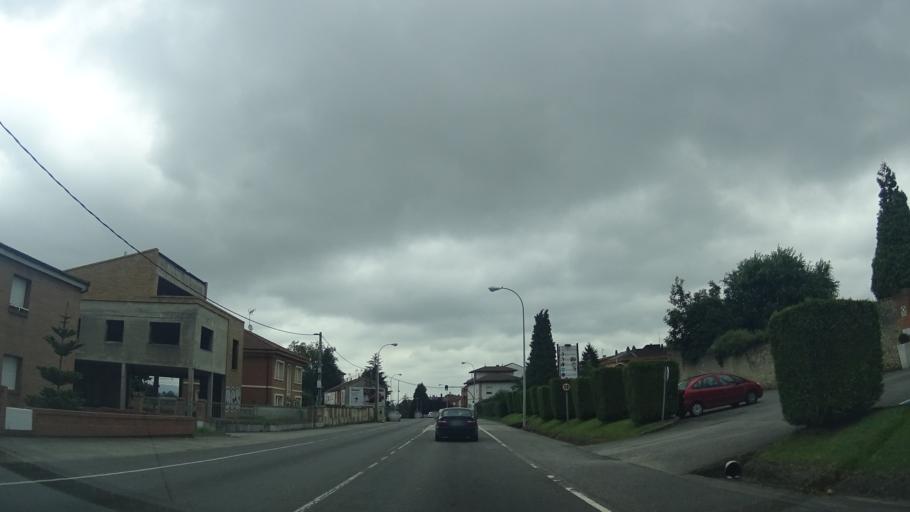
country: ES
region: Asturias
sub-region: Province of Asturias
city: Lugones
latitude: 43.3780
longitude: -5.8006
